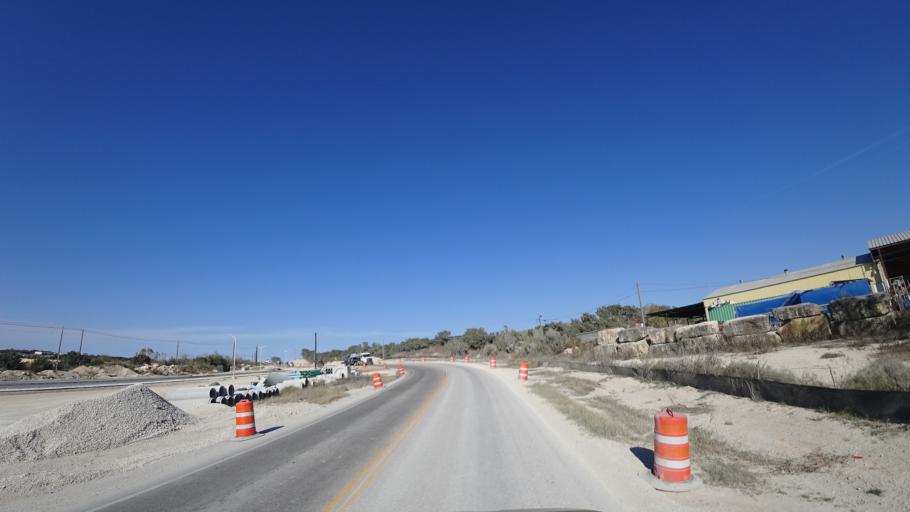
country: US
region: Texas
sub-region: Williamson County
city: Cedar Park
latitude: 30.5039
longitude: -97.8567
